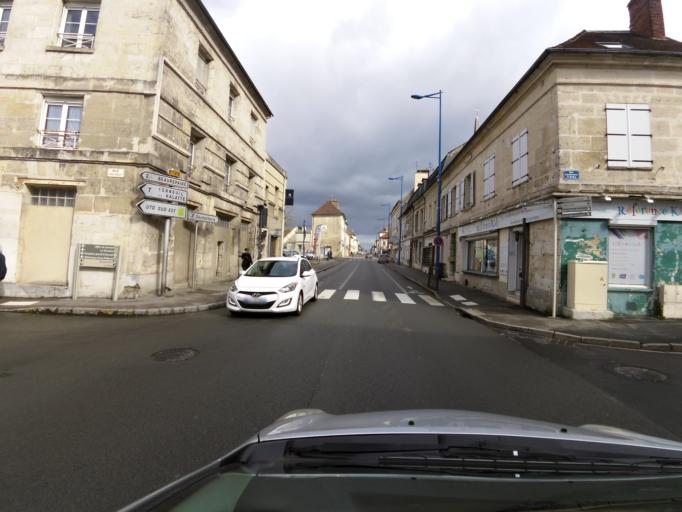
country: FR
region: Picardie
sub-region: Departement de l'Oise
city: Pont-Sainte-Maxence
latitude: 49.3004
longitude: 2.6045
